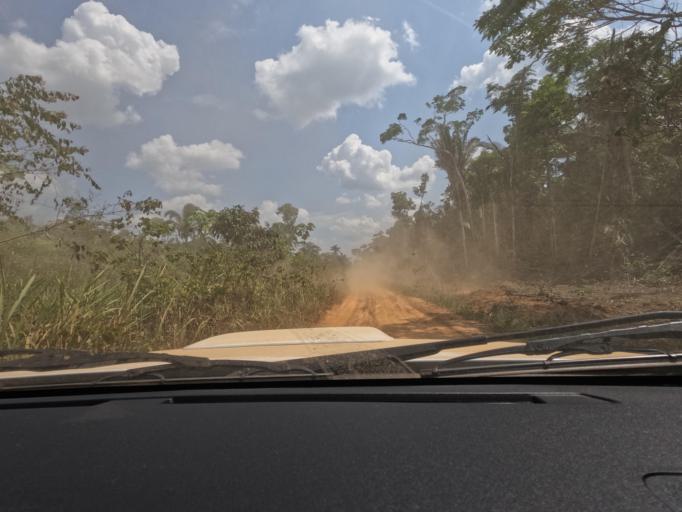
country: BR
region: Rondonia
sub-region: Porto Velho
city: Porto Velho
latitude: -8.6081
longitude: -64.2216
